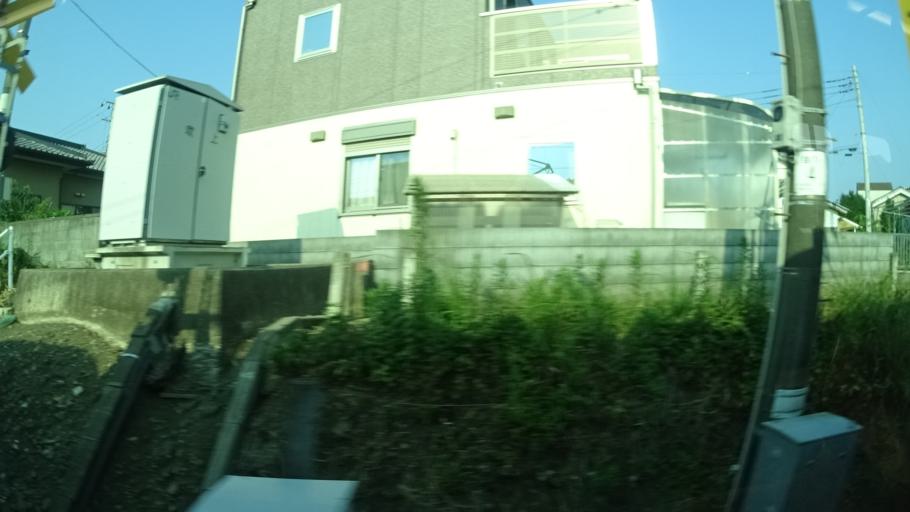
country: JP
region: Ibaraki
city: Hitachi
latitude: 36.6406
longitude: 140.6742
